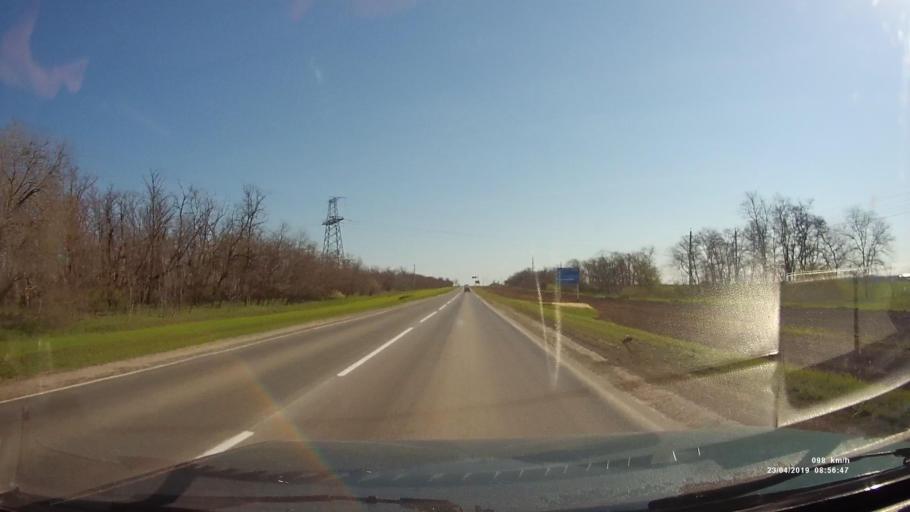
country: RU
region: Rostov
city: Sal'sk
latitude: 46.4966
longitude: 41.5136
